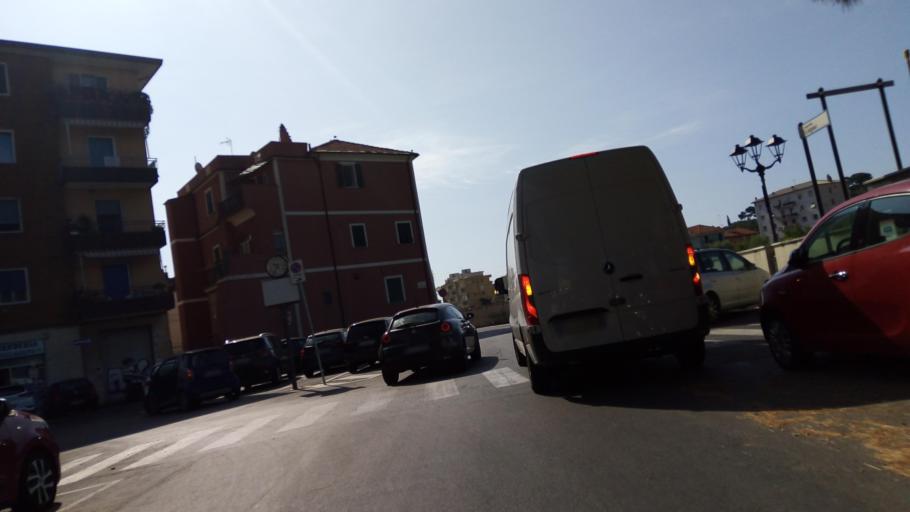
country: IT
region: Liguria
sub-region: Provincia di Savona
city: Albenga
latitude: 44.0493
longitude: 8.2101
